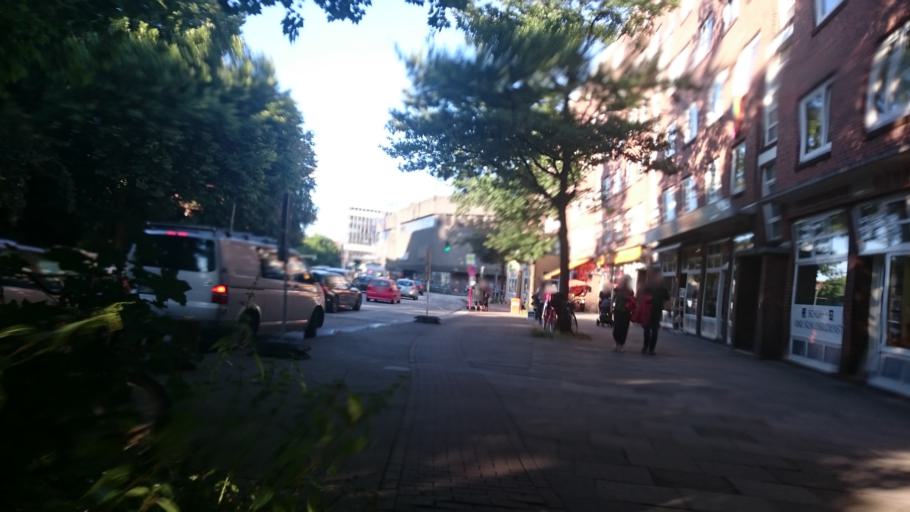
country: DE
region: Hamburg
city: St. Pauli
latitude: 53.5746
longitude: 9.9508
